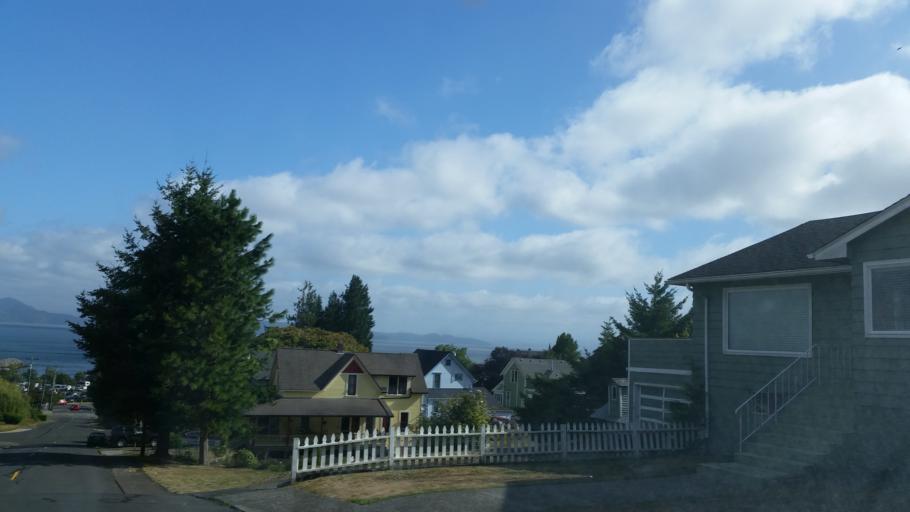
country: US
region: Oregon
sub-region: Clatsop County
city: Astoria
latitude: 46.1894
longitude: -123.8074
